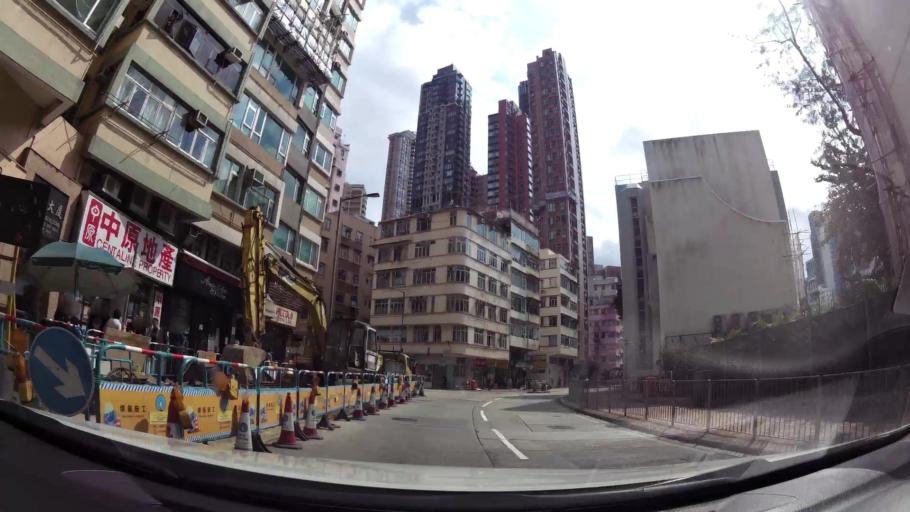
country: HK
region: Wanchai
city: Wan Chai
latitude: 22.2798
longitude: 114.1922
